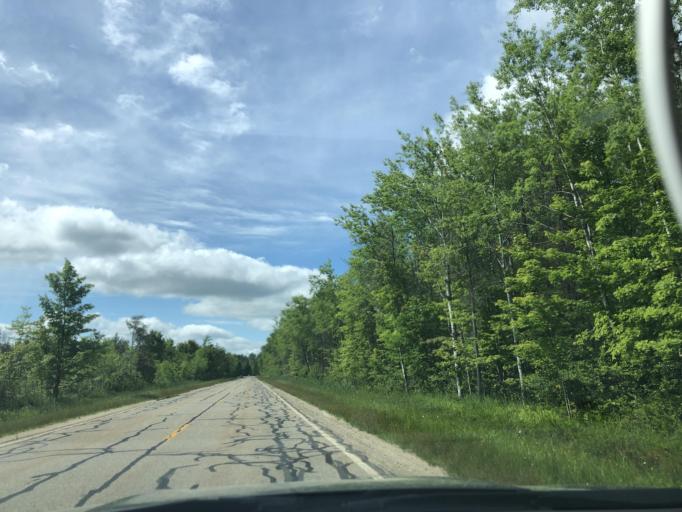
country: US
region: Michigan
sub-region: Roscommon County
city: Houghton Lake
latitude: 44.3408
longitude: -84.8545
